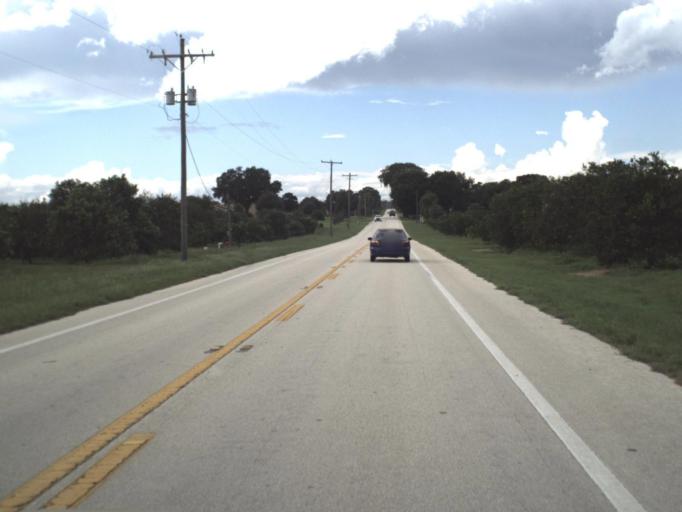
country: US
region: Florida
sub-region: Polk County
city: Fort Meade
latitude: 27.7481
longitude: -81.7367
